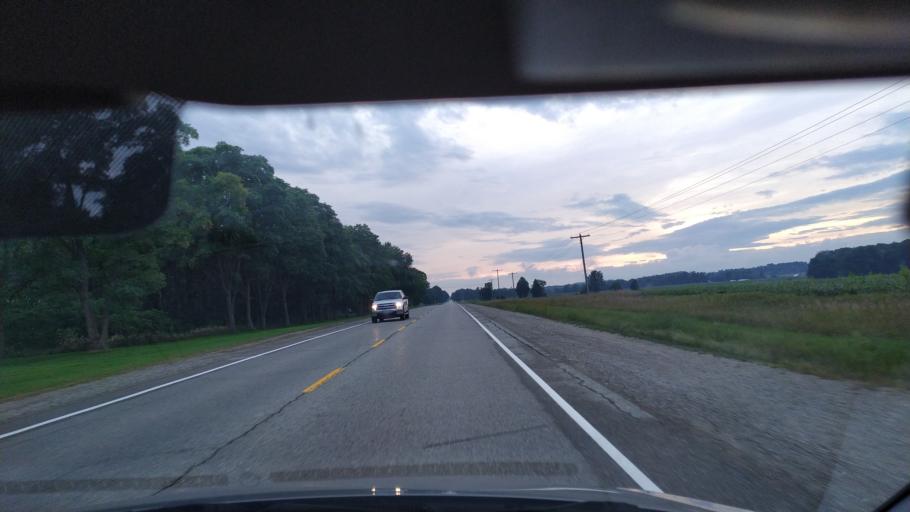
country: CA
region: Ontario
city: Kitchener
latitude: 43.3189
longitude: -80.5228
